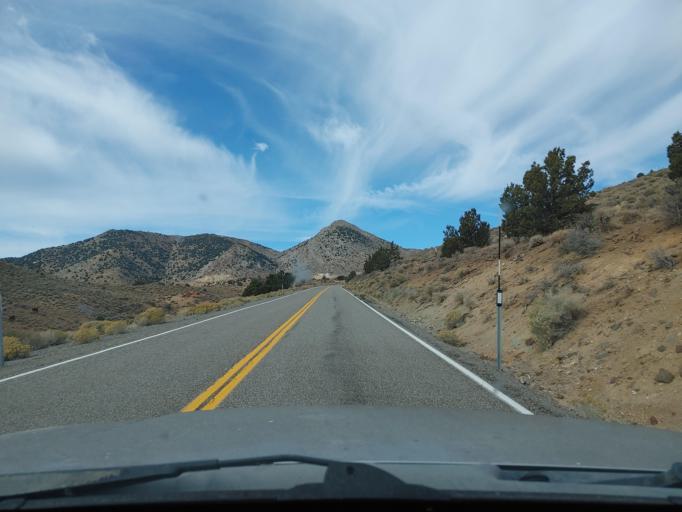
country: US
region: Nevada
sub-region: Storey County
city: Virginia City
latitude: 39.2870
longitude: -119.6389
